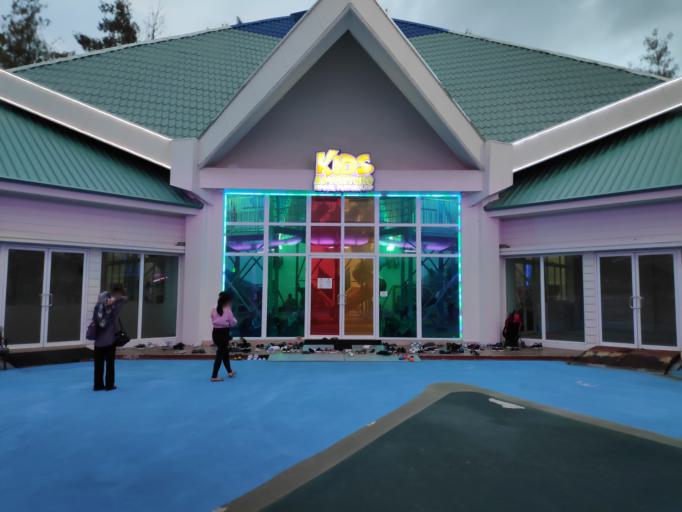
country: BN
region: Brunei and Muara
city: Bandar Seri Begawan
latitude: 4.9357
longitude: 114.8367
